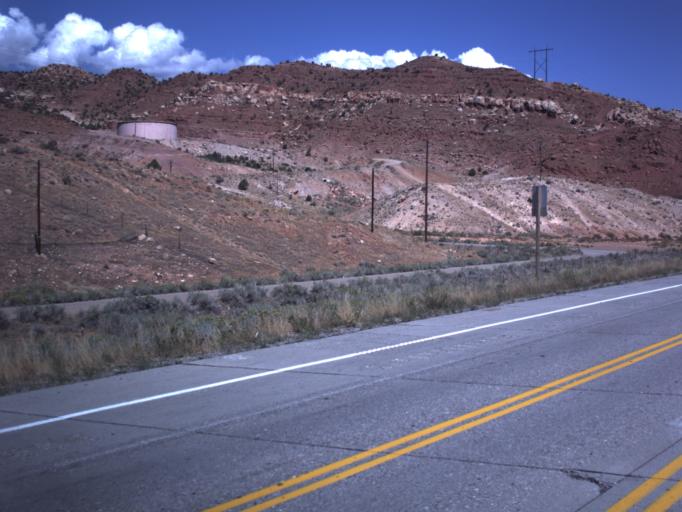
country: US
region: Utah
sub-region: Sevier County
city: Richfield
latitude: 38.7707
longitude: -112.1000
